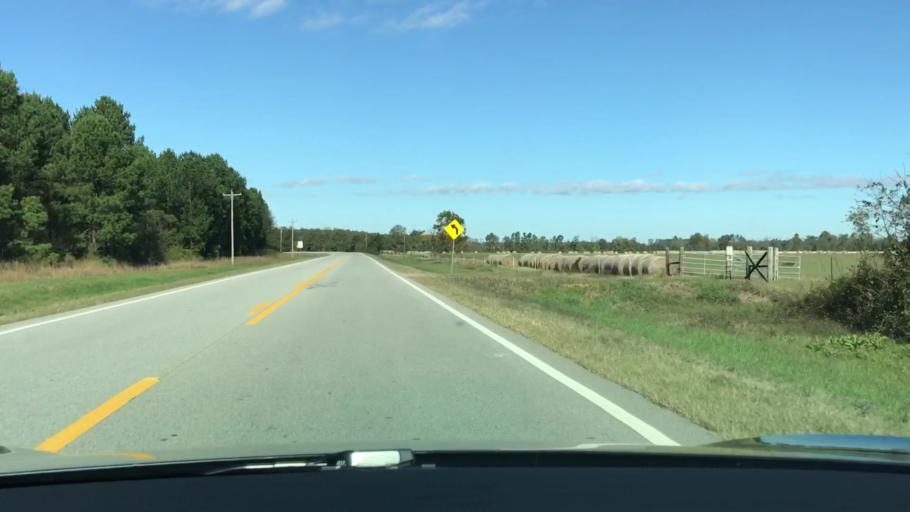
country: US
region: Georgia
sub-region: Glascock County
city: Gibson
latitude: 33.2931
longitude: -82.5114
